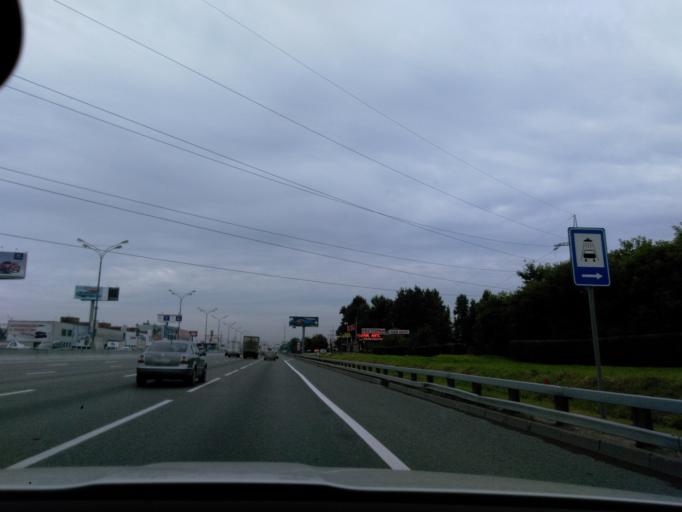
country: RU
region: Moscow
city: Ivanovskoye
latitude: 55.7598
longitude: 37.8424
